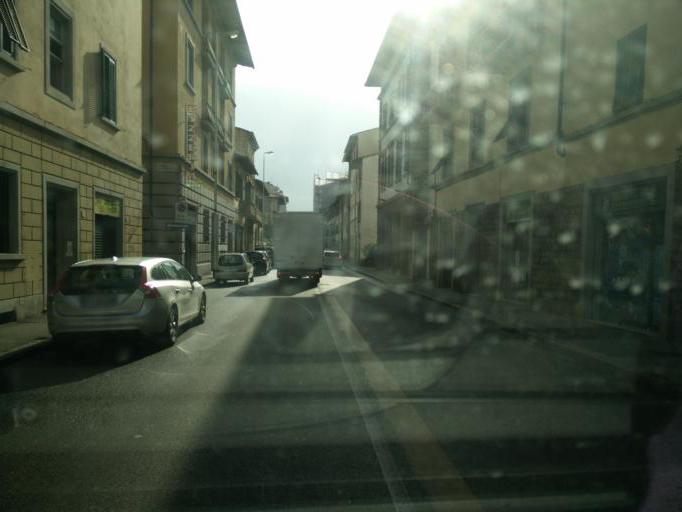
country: IT
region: Tuscany
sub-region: Province of Florence
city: Florence
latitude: 43.7838
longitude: 11.2324
